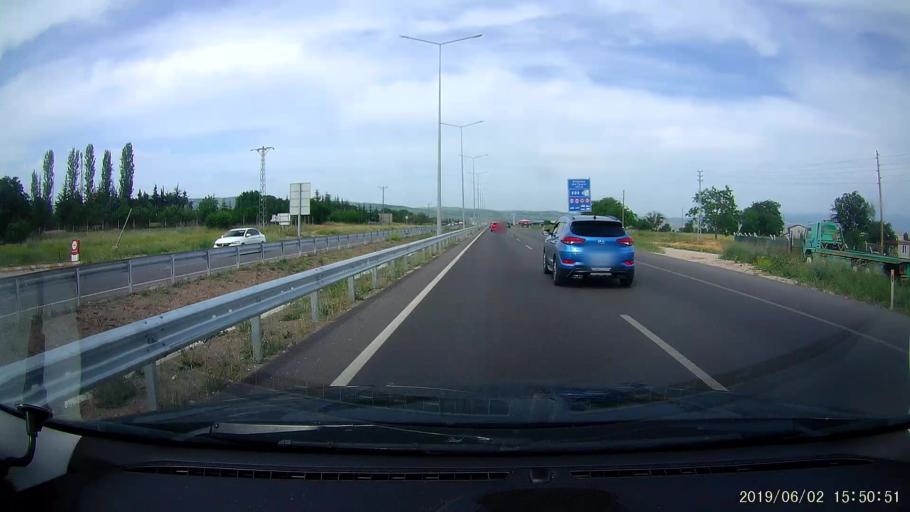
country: TR
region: Amasya
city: Merzifon
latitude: 40.8627
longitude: 35.4863
